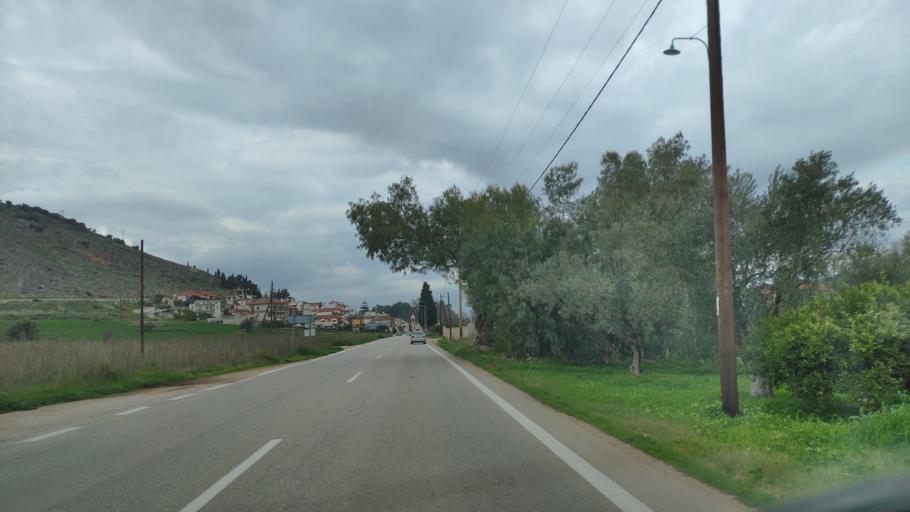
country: GR
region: Peloponnese
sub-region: Nomos Argolidos
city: Nea Kios
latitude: 37.5484
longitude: 22.7169
